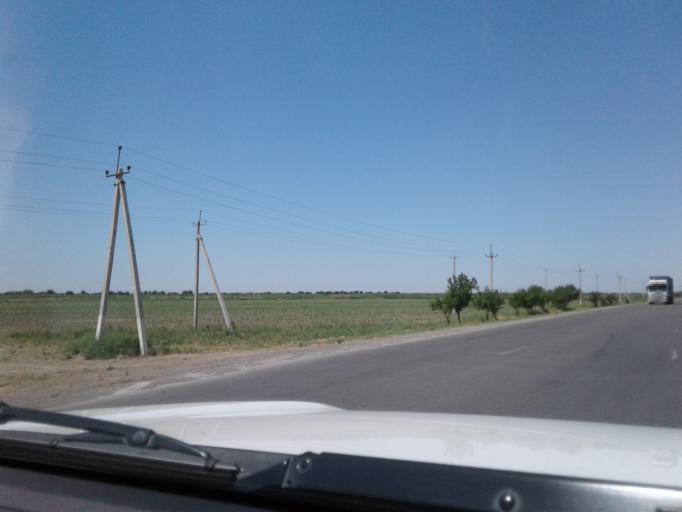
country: TM
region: Mary
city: Bayramaly
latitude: 37.6050
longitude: 62.2424
